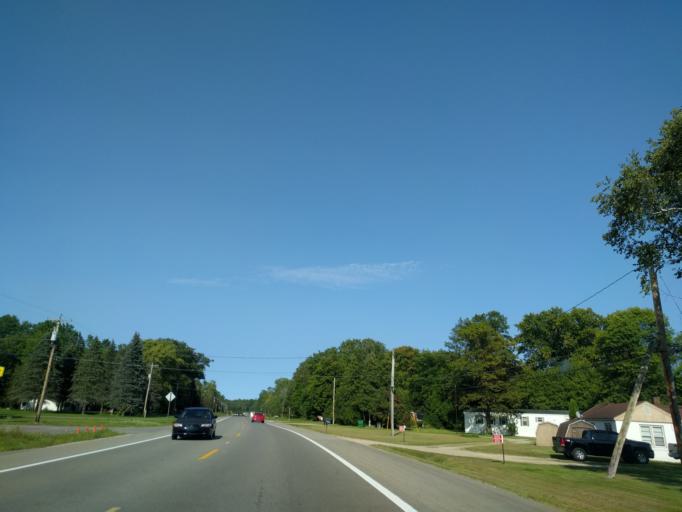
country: US
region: Michigan
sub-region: Menominee County
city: Menominee
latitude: 45.1524
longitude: -87.5984
